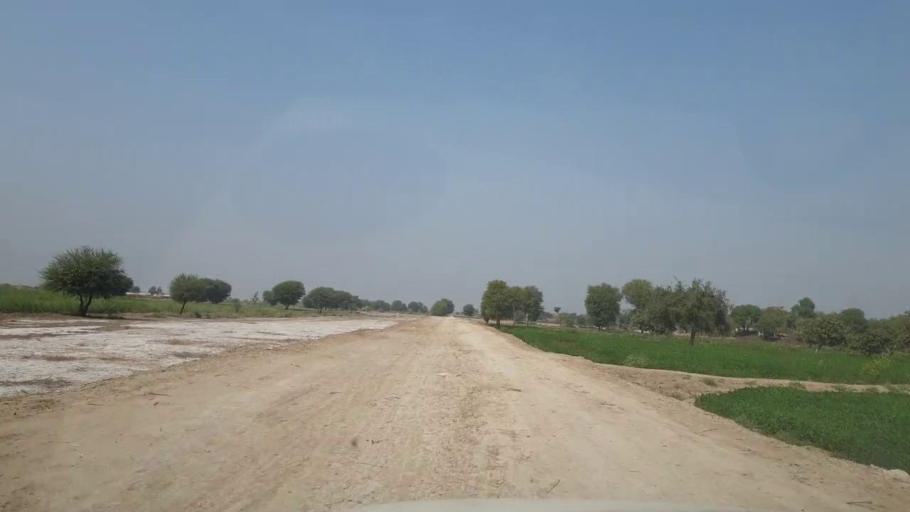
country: PK
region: Sindh
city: Mirpur Khas
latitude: 25.6561
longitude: 69.1349
